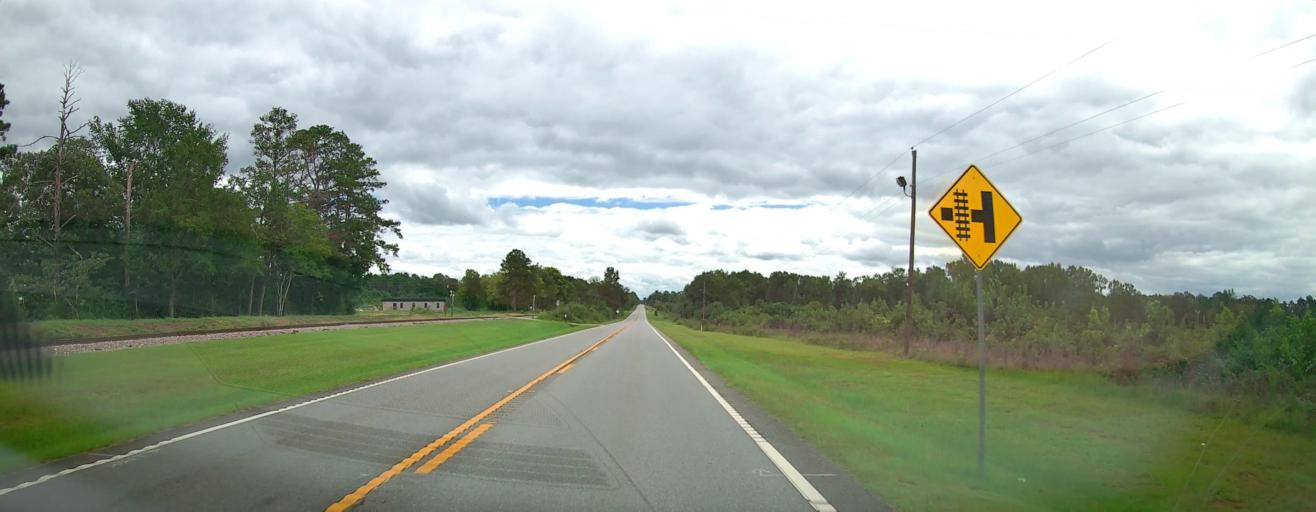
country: US
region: Georgia
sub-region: Twiggs County
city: Jeffersonville
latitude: 32.6778
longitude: -83.3351
